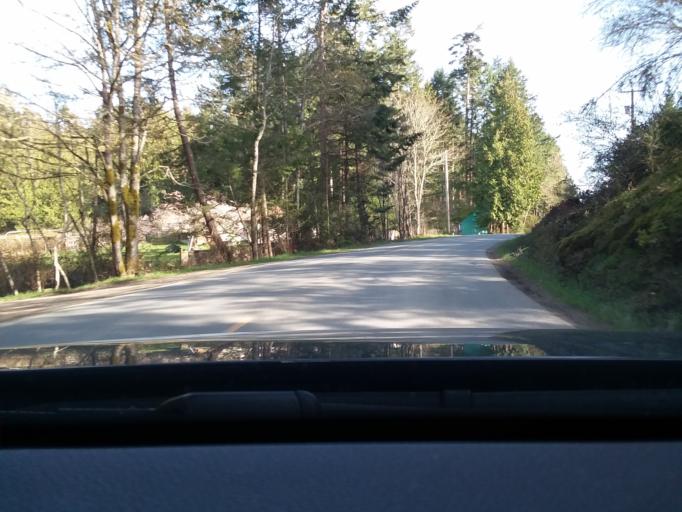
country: CA
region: British Columbia
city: North Saanich
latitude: 48.7841
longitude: -123.2810
